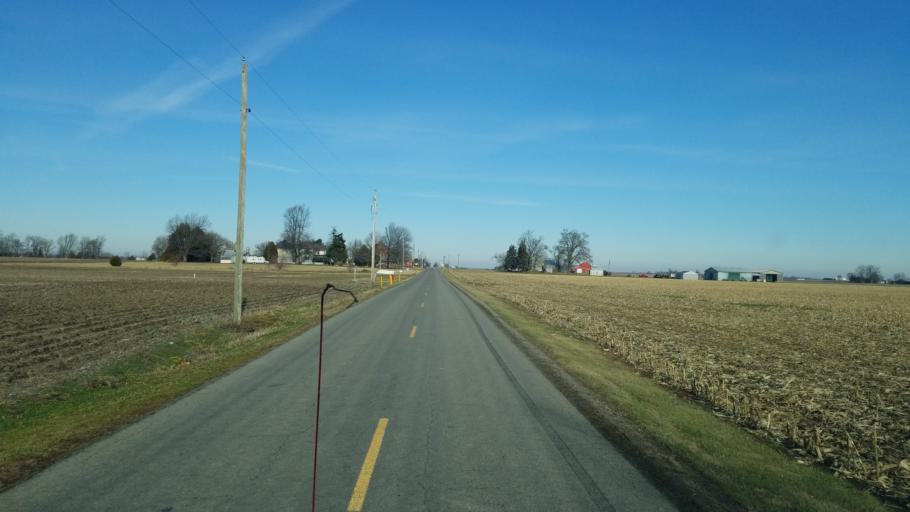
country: US
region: Ohio
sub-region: Putnam County
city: Pandora
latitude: 40.9444
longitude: -83.9380
